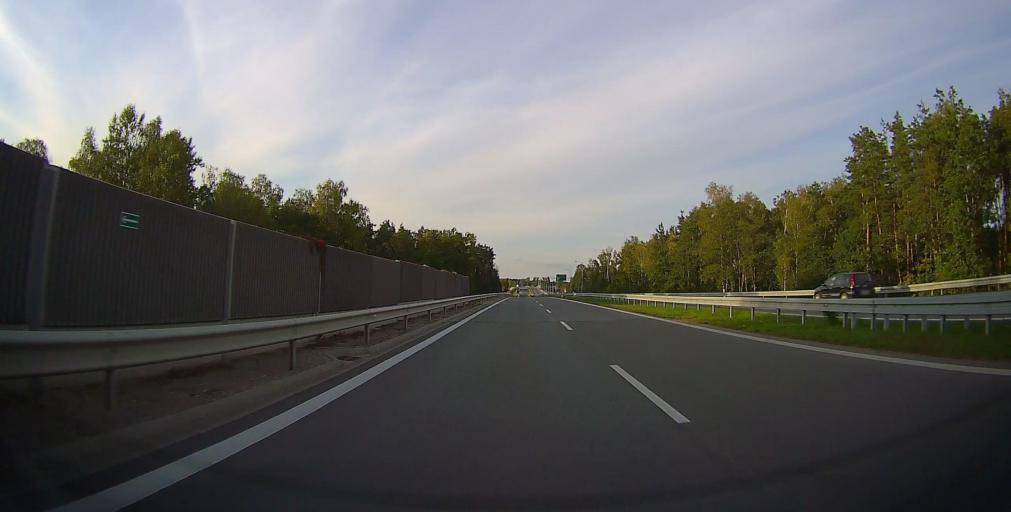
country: PL
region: Masovian Voivodeship
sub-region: Powiat piaseczynski
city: Baniocha
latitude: 51.9945
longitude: 21.1701
